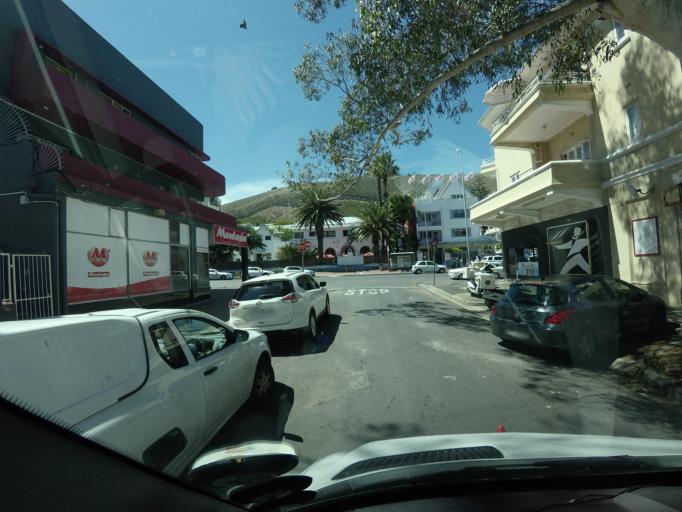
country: ZA
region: Western Cape
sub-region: City of Cape Town
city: Cape Town
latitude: -33.9121
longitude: 18.3903
